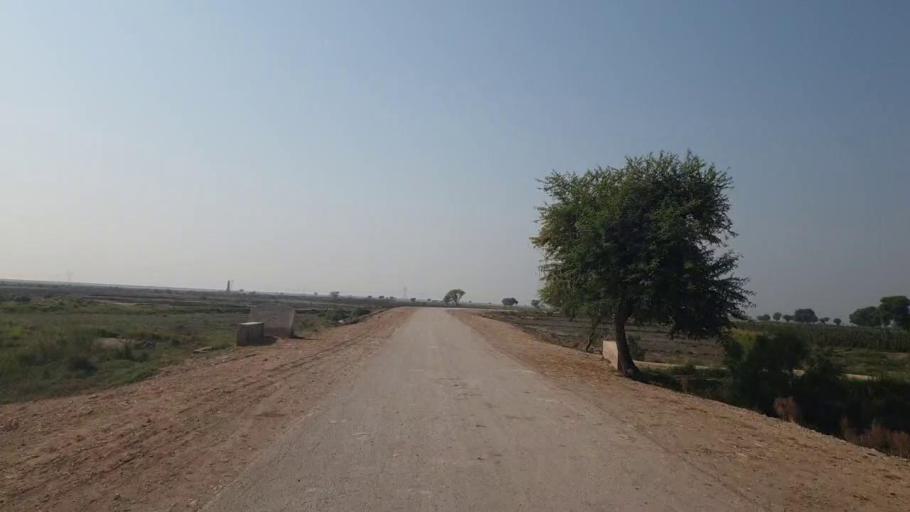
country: PK
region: Sindh
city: Sehwan
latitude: 26.4205
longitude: 67.8264
